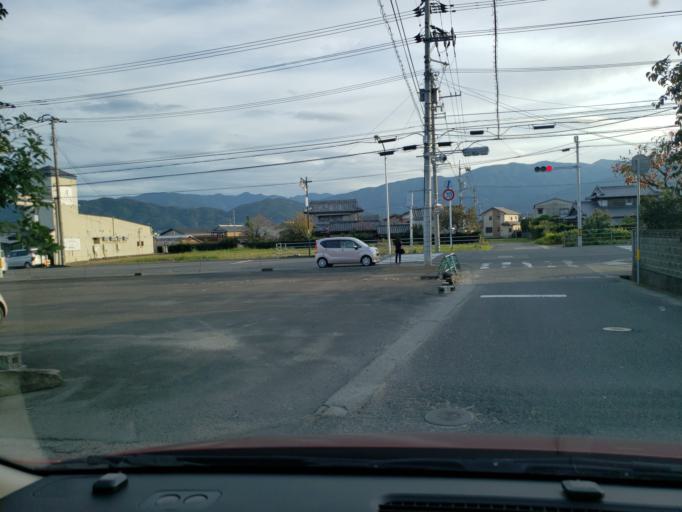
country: JP
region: Tokushima
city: Wakimachi
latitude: 34.0747
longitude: 134.2278
